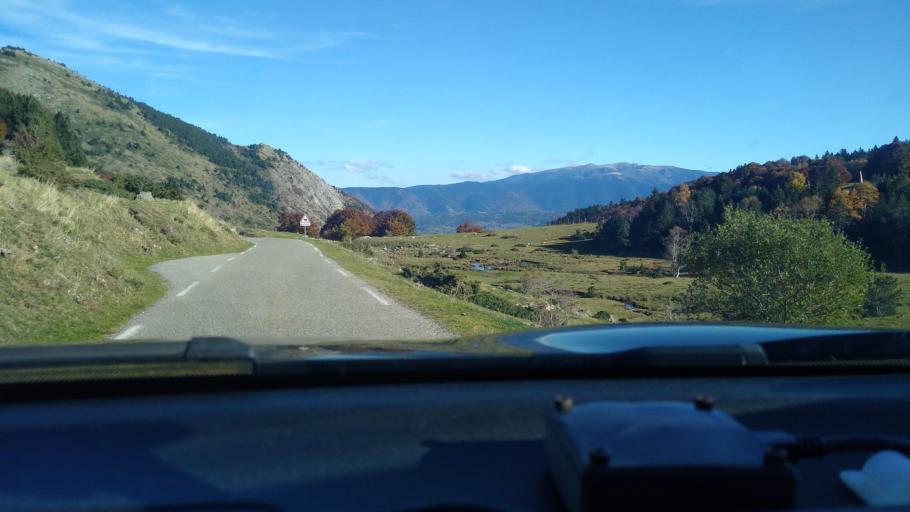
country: FR
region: Midi-Pyrenees
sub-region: Departement de l'Ariege
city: Ax-les-Thermes
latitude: 42.7289
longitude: 2.0093
